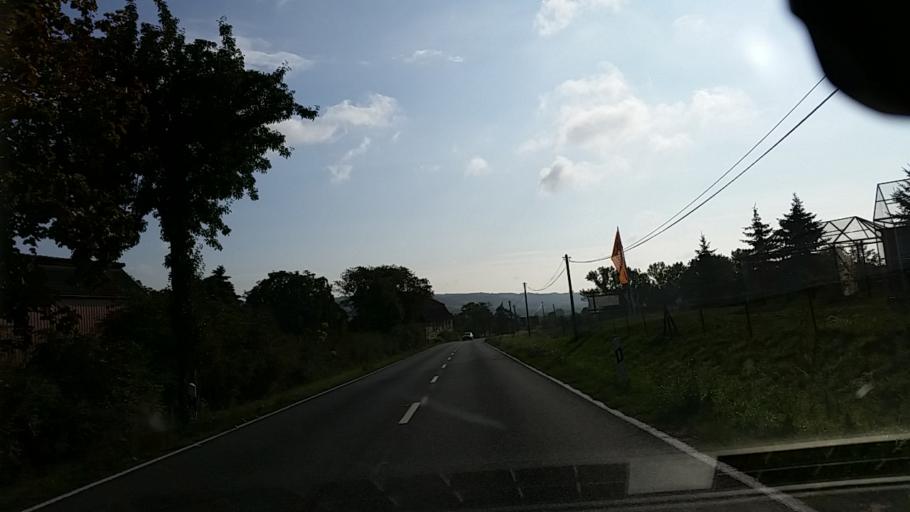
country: DE
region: Saxony-Anhalt
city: Kelbra
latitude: 51.3691
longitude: 11.0060
